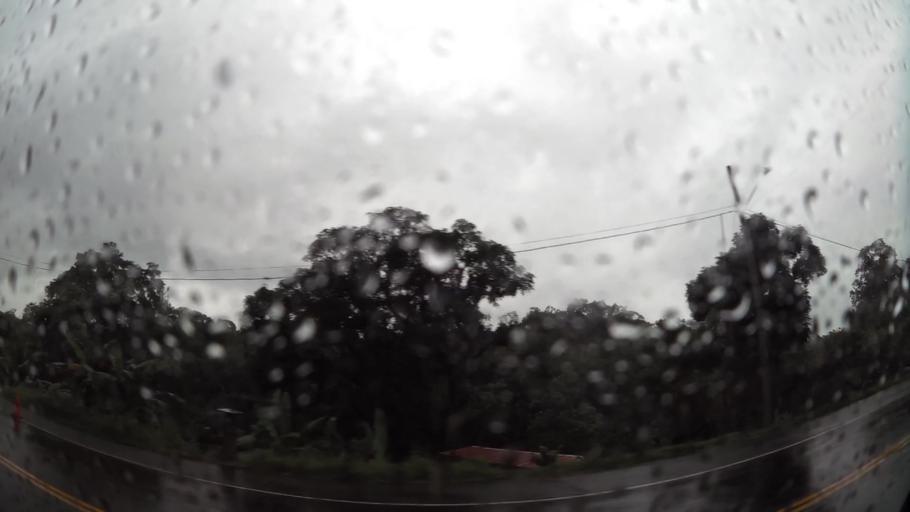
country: PA
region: Colon
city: Quebrada Bonita Adentro
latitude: 9.2867
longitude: -79.7186
